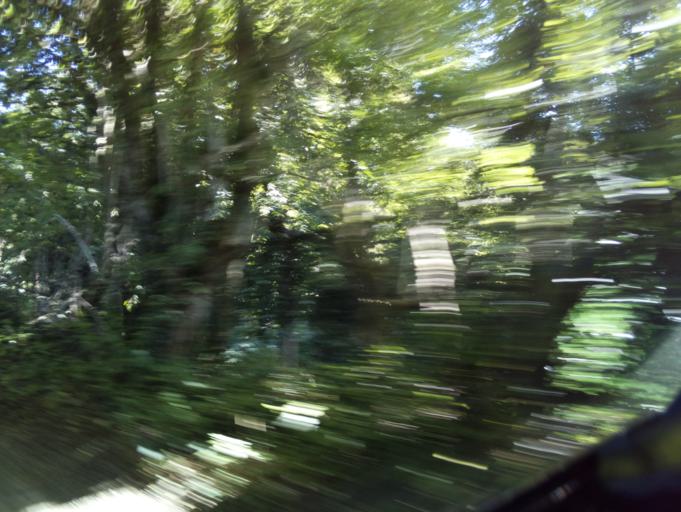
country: GB
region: Wales
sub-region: Torfaen County Borough
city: Cwmbran
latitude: 51.6224
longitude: -3.0376
